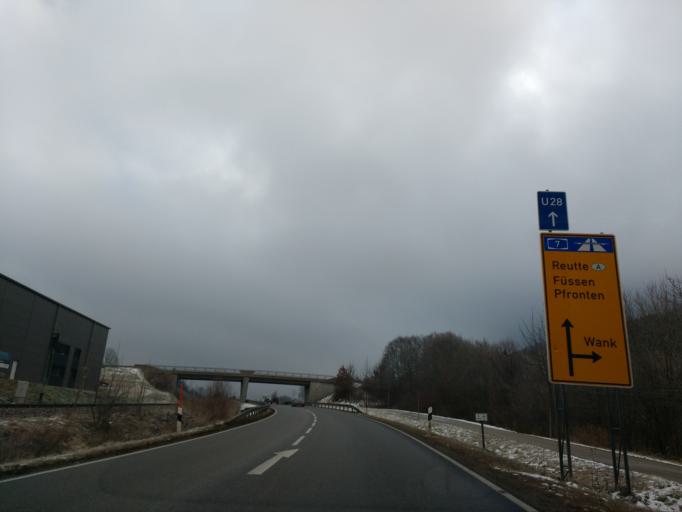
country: DE
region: Bavaria
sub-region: Swabia
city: Nesselwang
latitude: 47.6159
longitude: 10.5161
